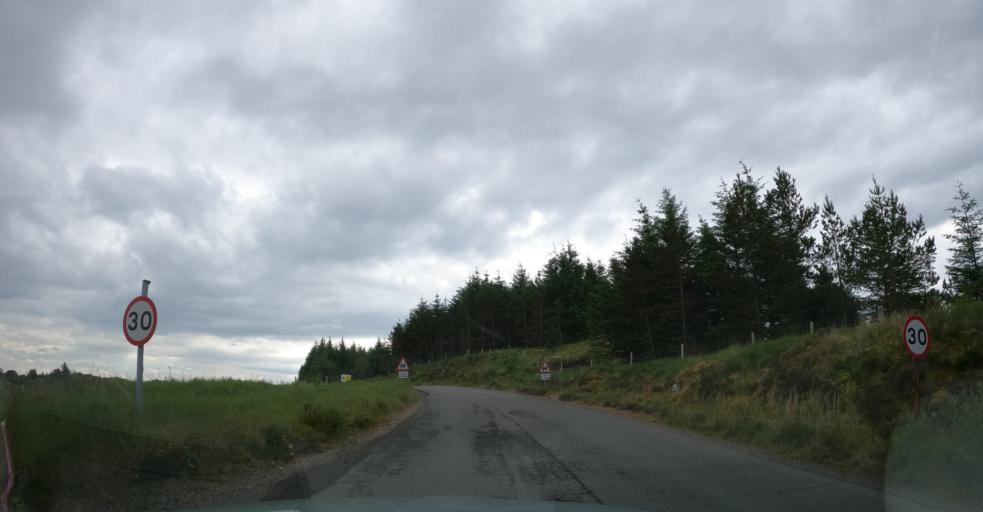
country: GB
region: Scotland
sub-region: Eilean Siar
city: Stornoway
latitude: 58.2033
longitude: -6.4209
